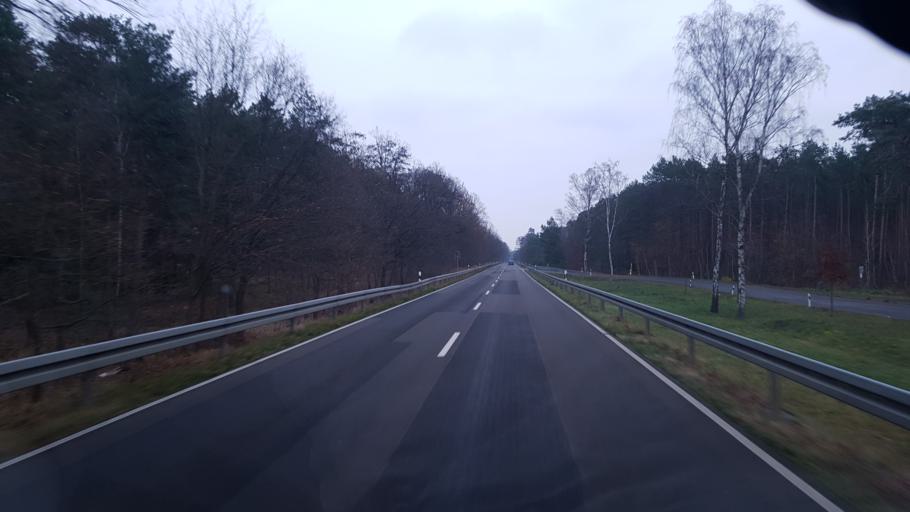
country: DE
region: Brandenburg
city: Tauer
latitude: 51.9081
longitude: 14.4799
